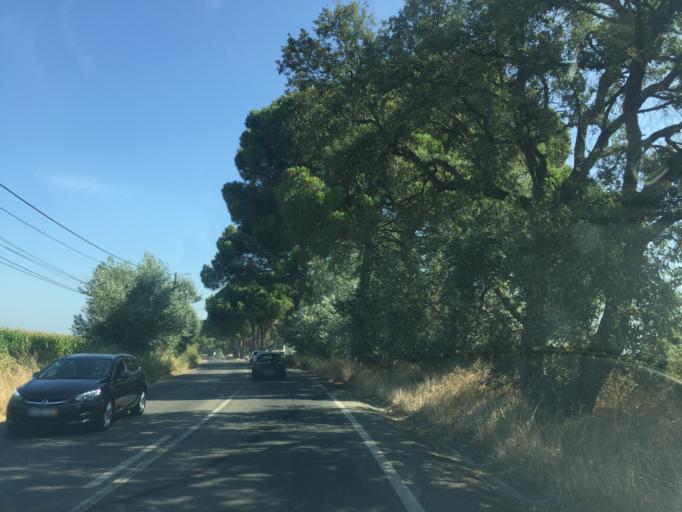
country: PT
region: Santarem
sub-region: Almeirim
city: Almeirim
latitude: 39.2243
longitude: -8.6084
